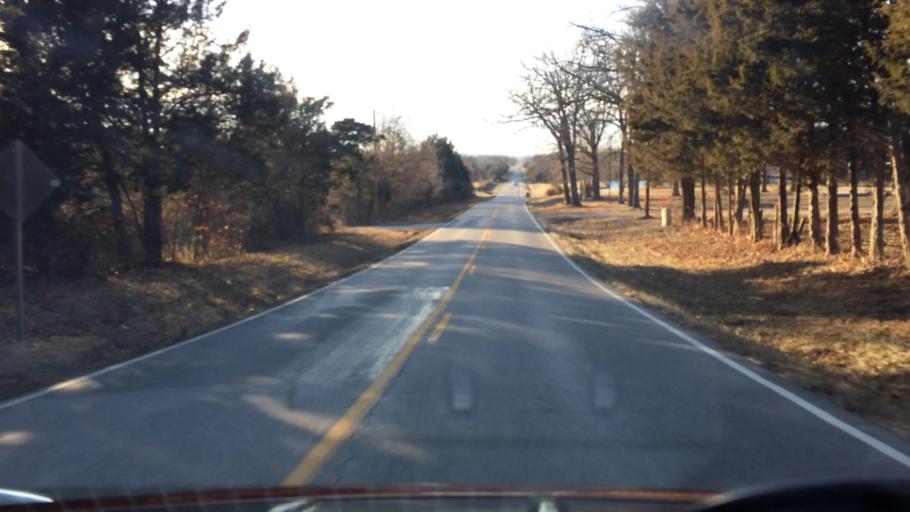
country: US
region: Missouri
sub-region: Webster County
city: Marshfield
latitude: 37.3409
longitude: -92.9793
